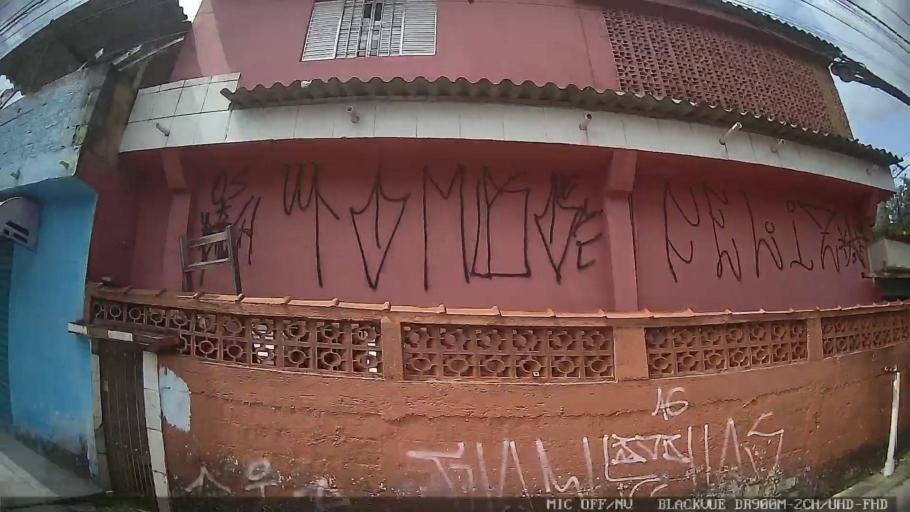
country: BR
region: Sao Paulo
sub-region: Poa
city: Poa
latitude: -23.5329
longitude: -46.3324
